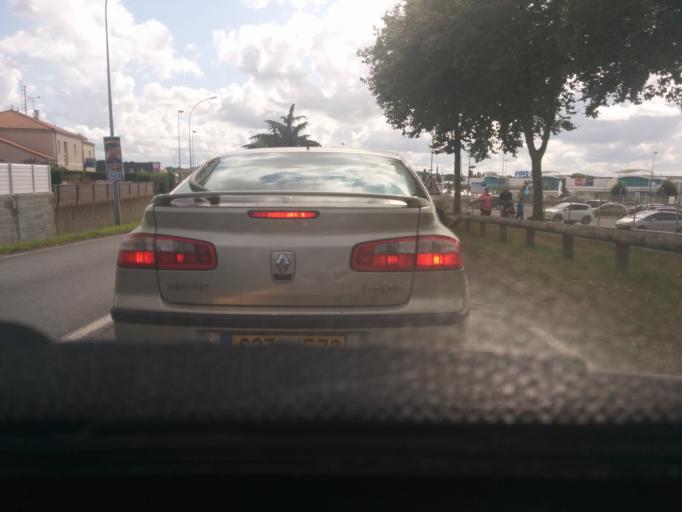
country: FR
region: Pays de la Loire
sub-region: Departement de la Vendee
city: Les Herbiers
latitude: 46.8759
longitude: -1.0237
